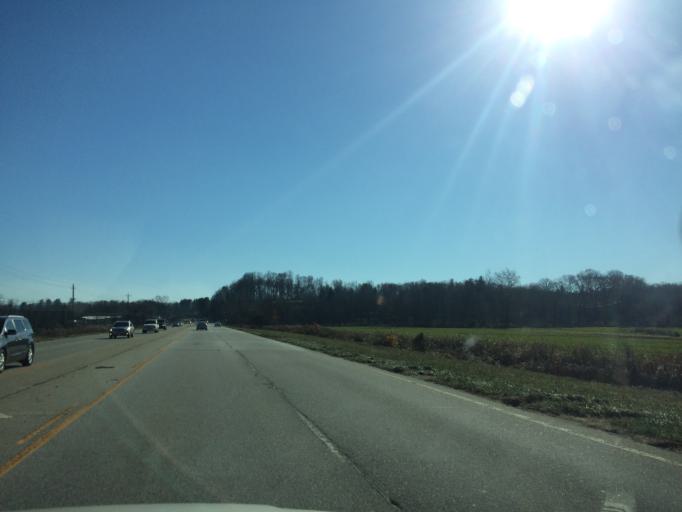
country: US
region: North Carolina
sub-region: Henderson County
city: Mills River
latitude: 35.3956
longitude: -82.5692
